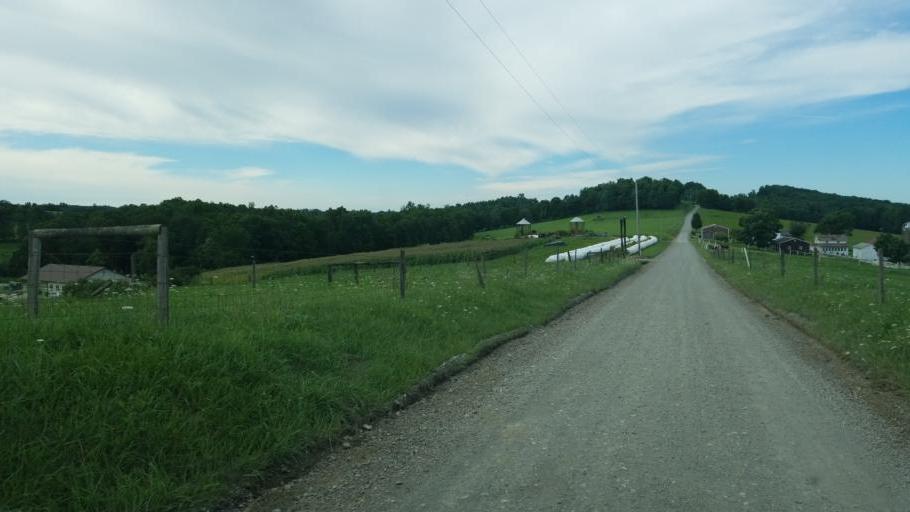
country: US
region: Ohio
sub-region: Holmes County
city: Millersburg
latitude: 40.5119
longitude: -81.8429
